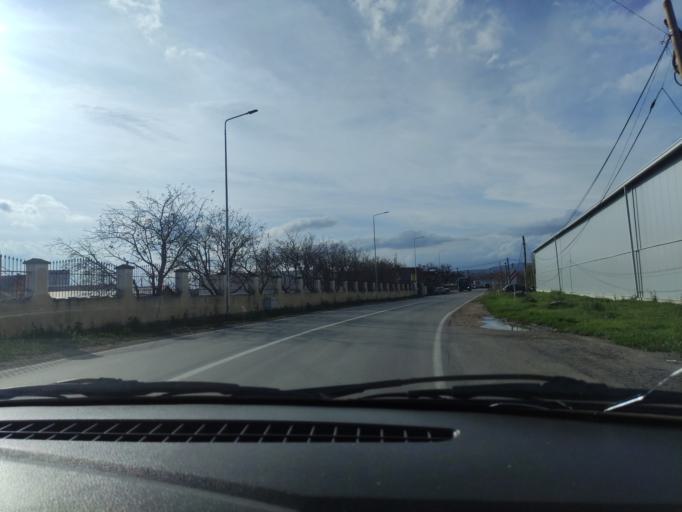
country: RO
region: Brasov
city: Codlea
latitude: 45.7057
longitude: 25.4589
